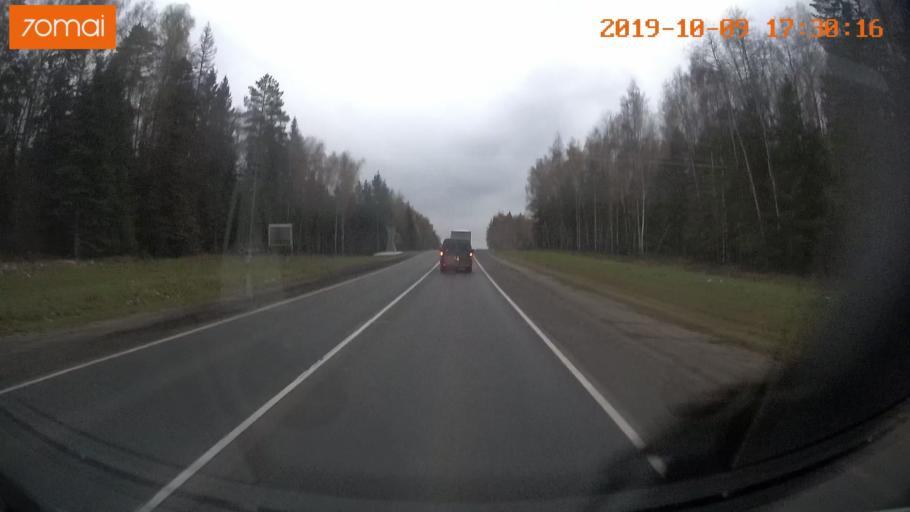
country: RU
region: Ivanovo
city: Bogorodskoye
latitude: 57.1439
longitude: 41.0510
